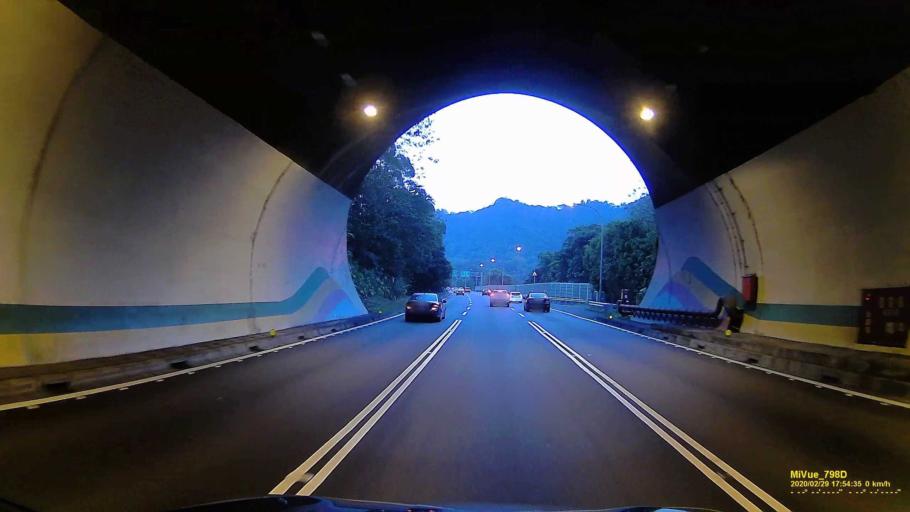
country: TW
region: Taipei
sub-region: Taipei
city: Banqiao
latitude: 24.9832
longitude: 121.4946
